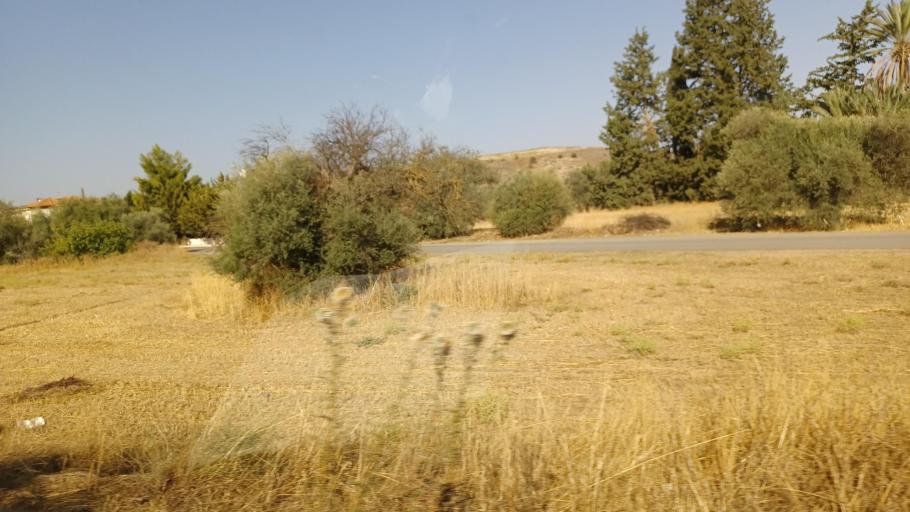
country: CY
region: Lefkosia
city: Alampra
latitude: 34.9922
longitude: 33.3661
